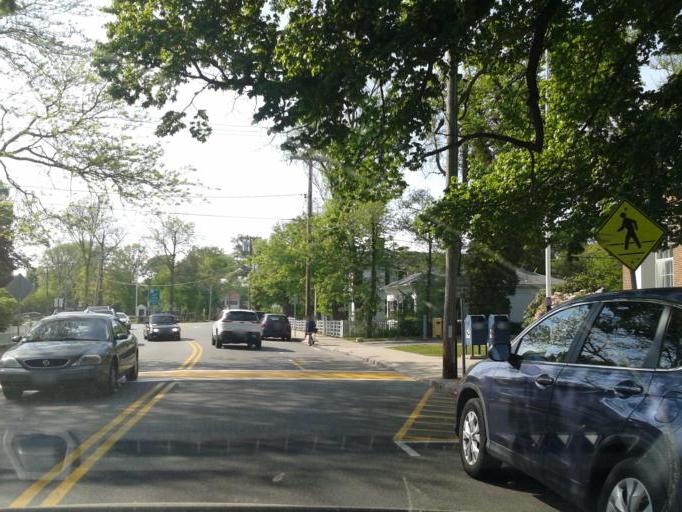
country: US
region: Massachusetts
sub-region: Barnstable County
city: Falmouth
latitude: 41.5532
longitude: -70.6179
